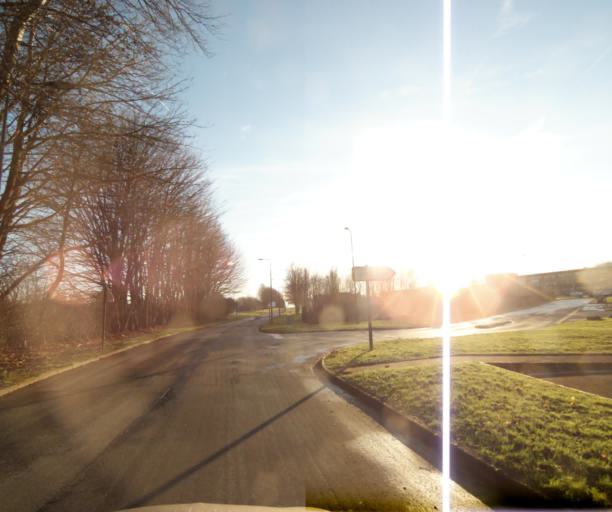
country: FR
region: Nord-Pas-de-Calais
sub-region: Departement du Nord
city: Famars
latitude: 50.3245
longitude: 3.5166
